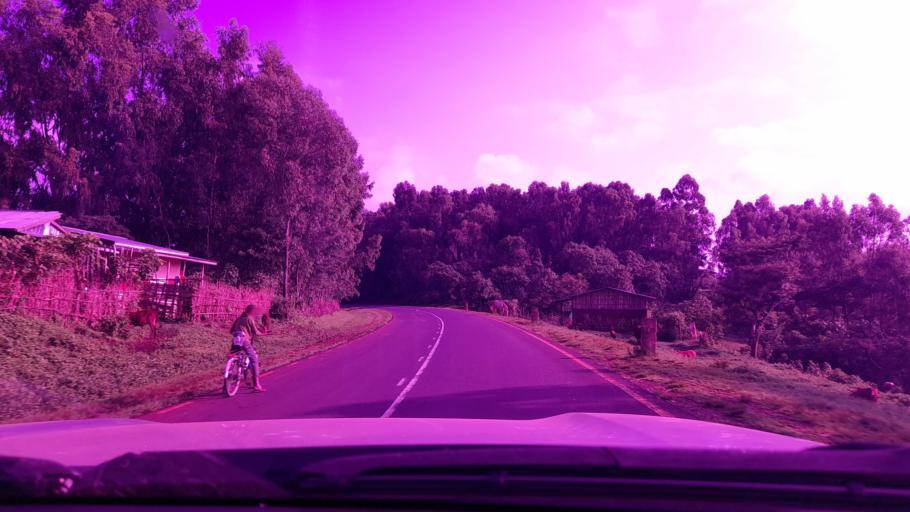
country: ET
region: Oromiya
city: Bedele
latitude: 8.1607
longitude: 36.4750
